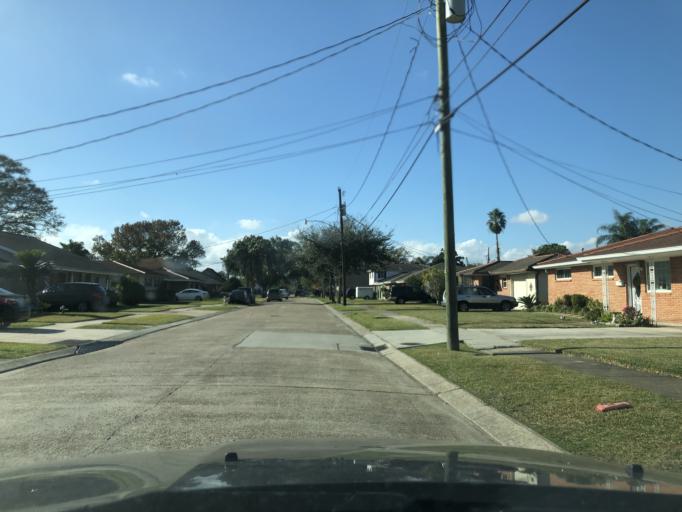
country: US
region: Louisiana
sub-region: Jefferson Parish
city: Metairie Terrace
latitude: 29.9862
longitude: -90.1630
